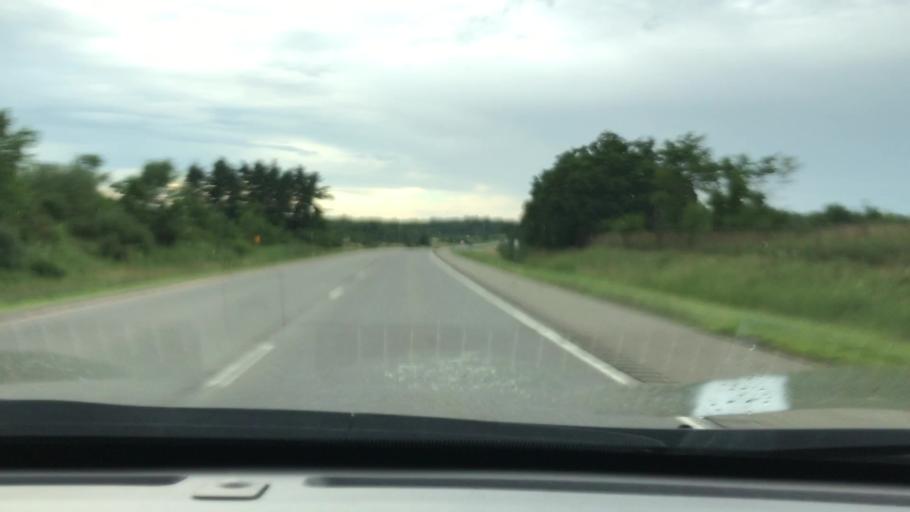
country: US
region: New York
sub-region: Erie County
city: North Boston
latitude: 42.6132
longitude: -78.7600
